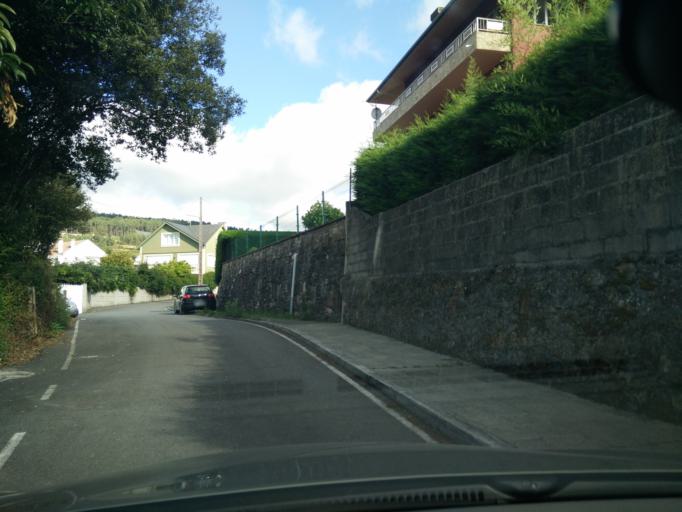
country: ES
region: Galicia
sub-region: Provincia da Coruna
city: Laxe
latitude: 43.2184
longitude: -8.9327
